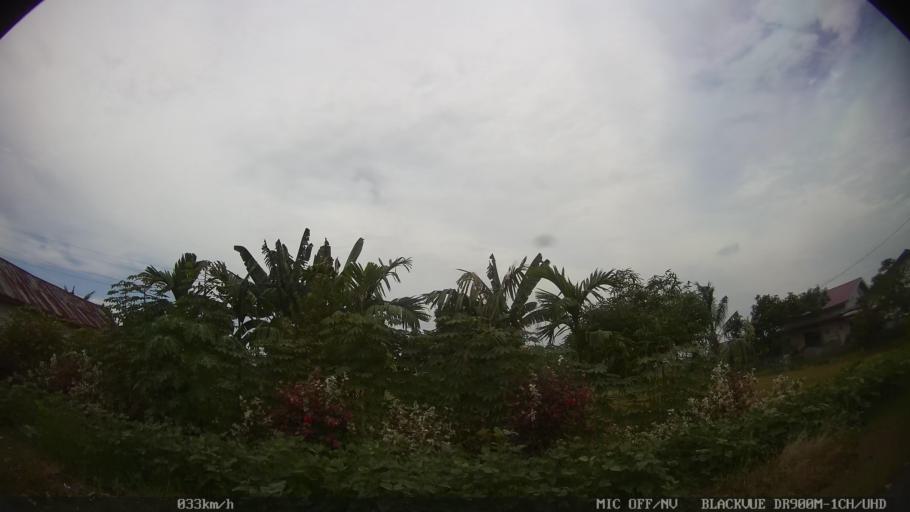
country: ID
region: North Sumatra
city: Sunggal
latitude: 3.6180
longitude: 98.5966
